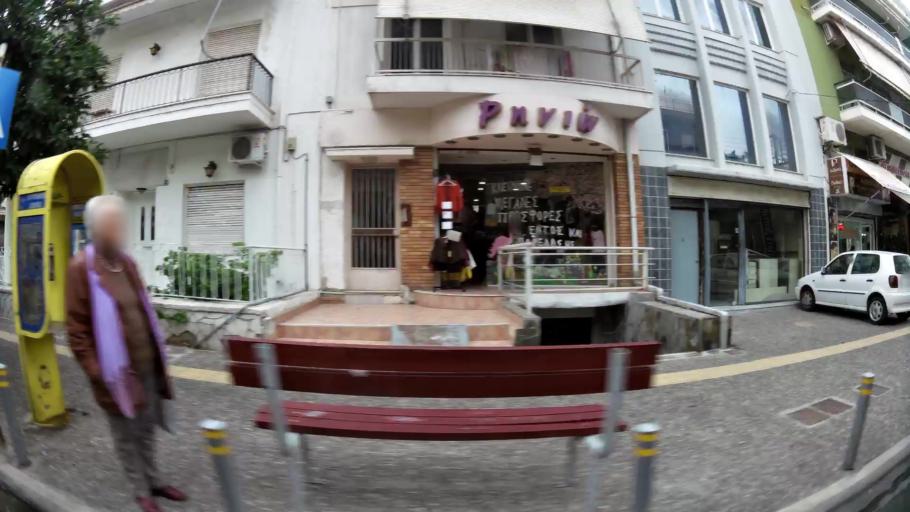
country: GR
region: Attica
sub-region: Nomos Piraios
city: Korydallos
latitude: 37.9802
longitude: 23.6379
